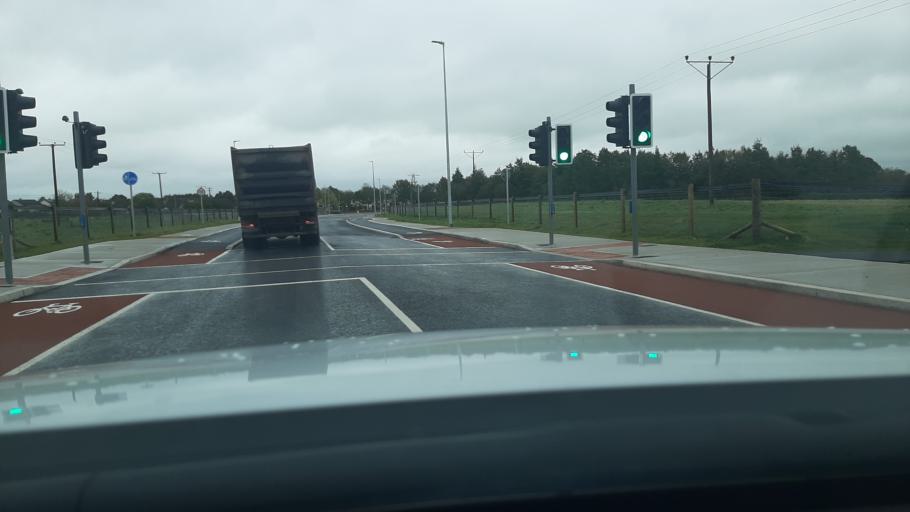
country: IE
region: Leinster
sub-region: Kildare
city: Kildare
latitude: 53.1643
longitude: -6.9167
